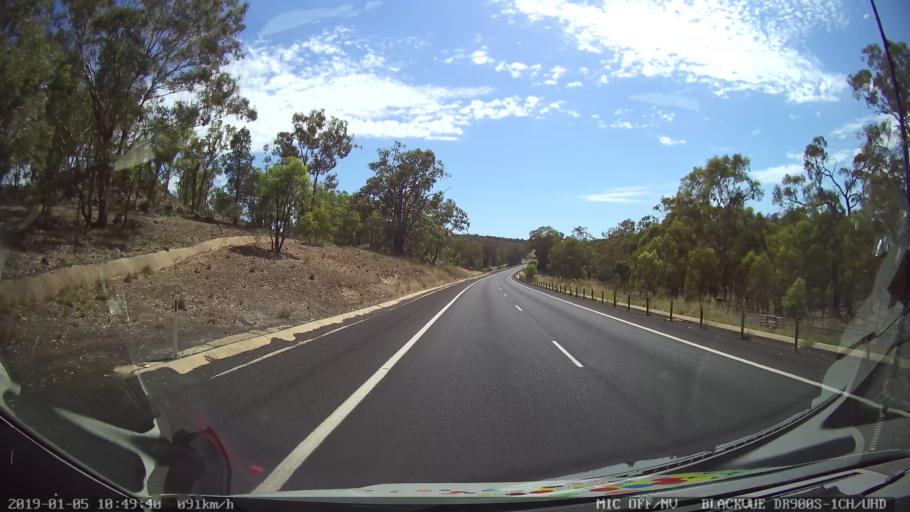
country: AU
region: New South Wales
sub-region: Warrumbungle Shire
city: Coonabarabran
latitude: -31.4325
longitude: 149.0641
